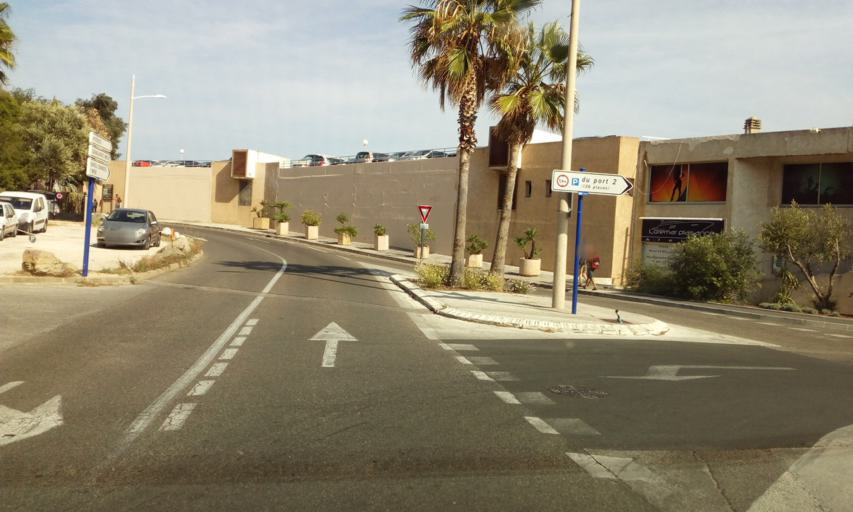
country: FR
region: Provence-Alpes-Cote d'Azur
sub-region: Departement du Var
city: Le Lavandou
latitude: 43.1377
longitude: 6.3766
